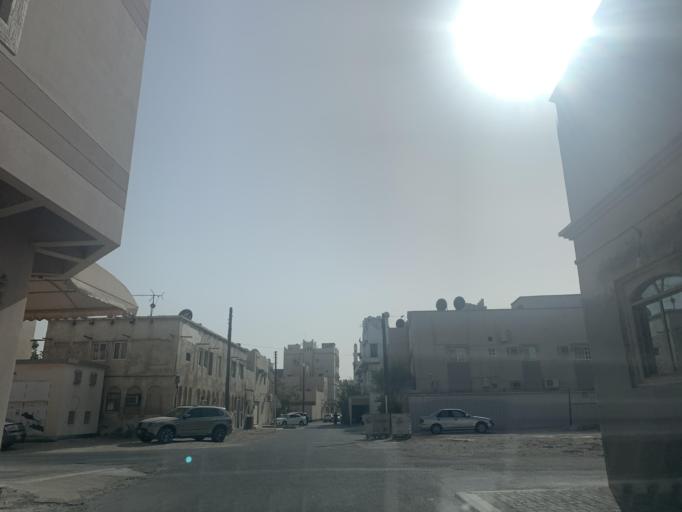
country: BH
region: Northern
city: Sitrah
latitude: 26.1634
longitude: 50.6181
